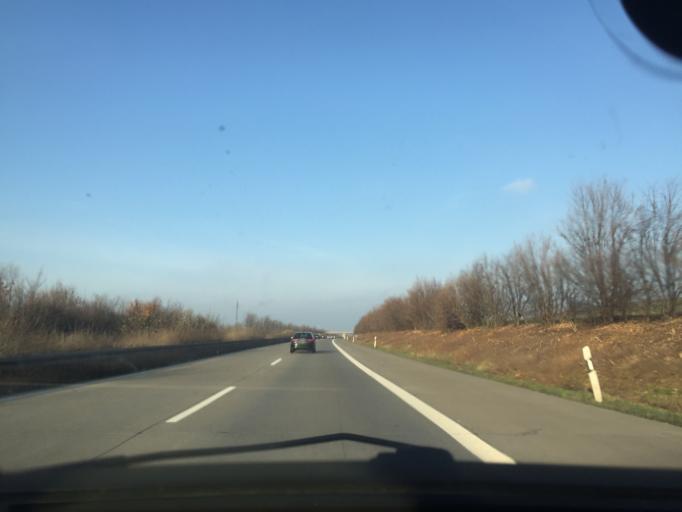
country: DE
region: Saxony-Anhalt
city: Hohendodeleben
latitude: 52.0968
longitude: 11.5309
